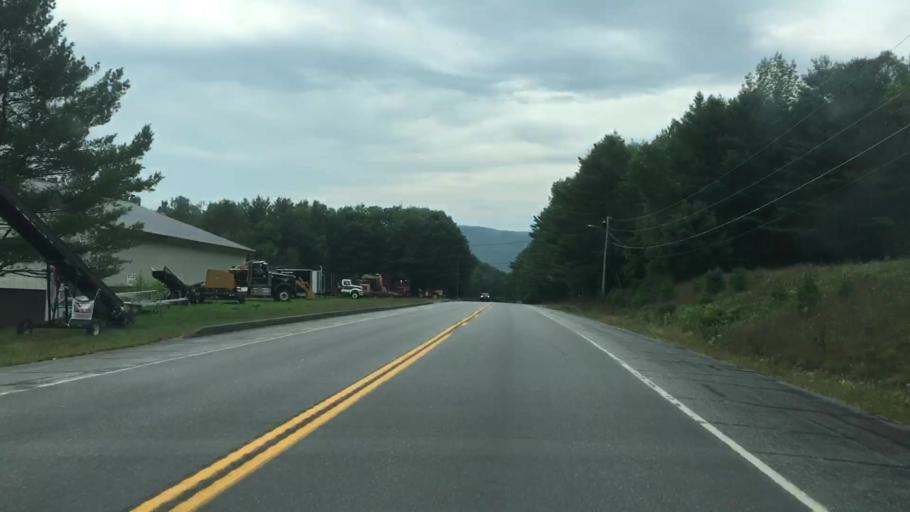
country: US
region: Maine
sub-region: Oxford County
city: Bethel
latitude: 44.4867
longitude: -70.7541
